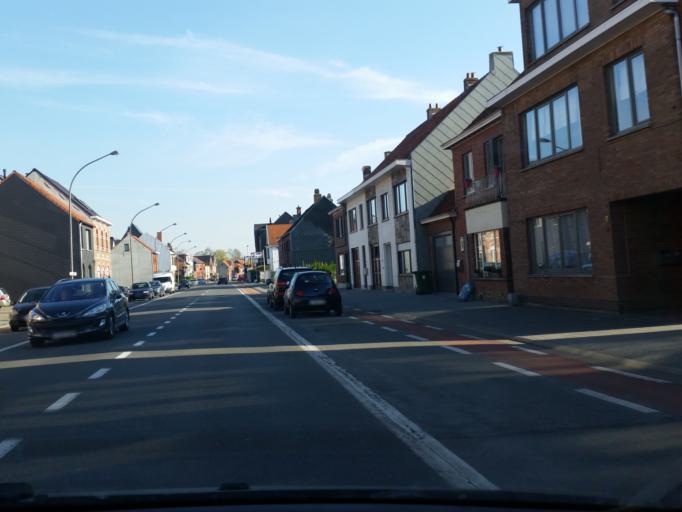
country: BE
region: Flanders
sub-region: Provincie Oost-Vlaanderen
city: Stekene
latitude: 51.2091
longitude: 4.0740
